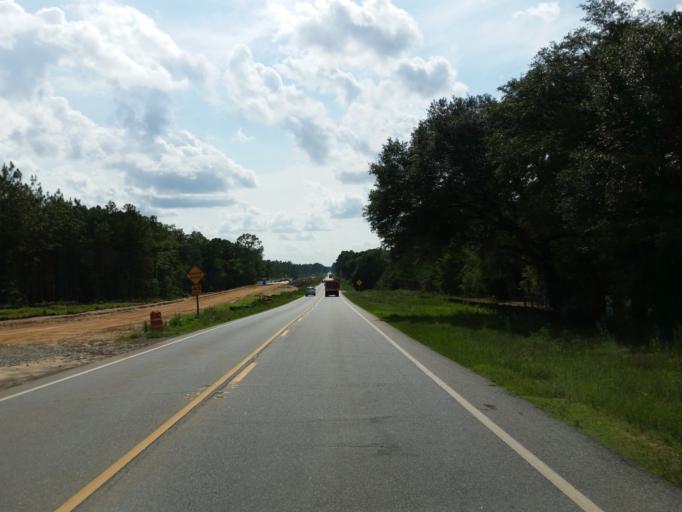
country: US
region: Georgia
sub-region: Lee County
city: Leesburg
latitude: 31.7250
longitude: -84.0142
